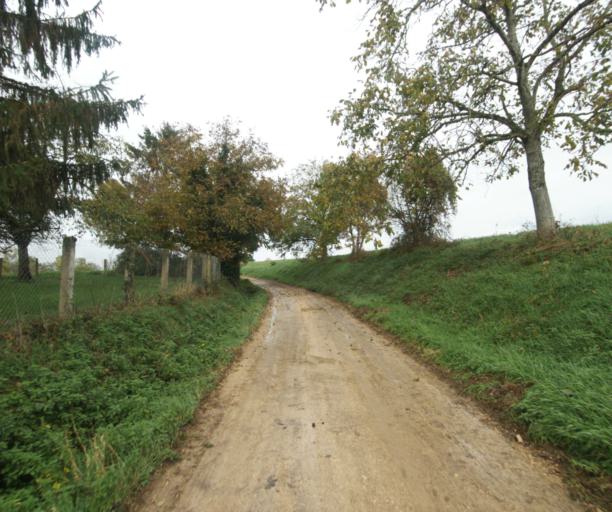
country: FR
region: Rhone-Alpes
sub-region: Departement de l'Ain
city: Pont-de-Vaux
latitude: 46.4763
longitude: 4.8923
